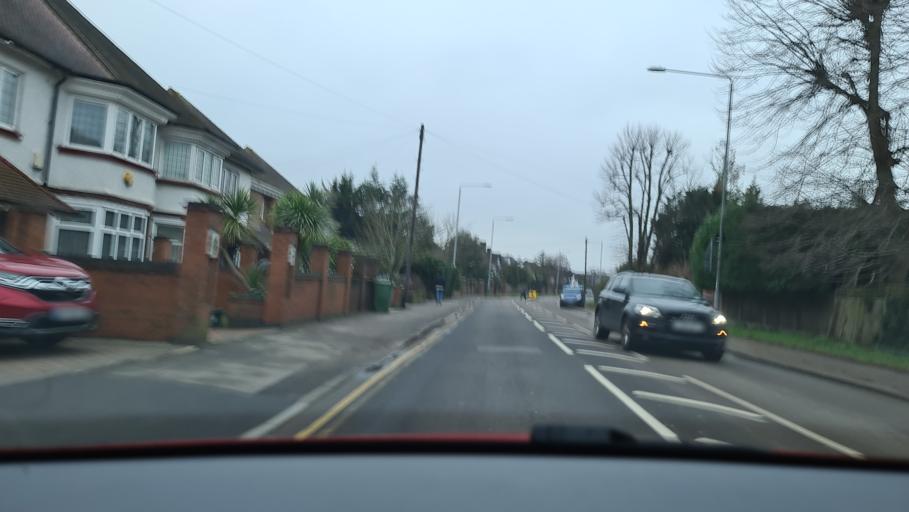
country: GB
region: England
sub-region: Greater London
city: New Malden
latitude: 51.4132
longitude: -0.2751
